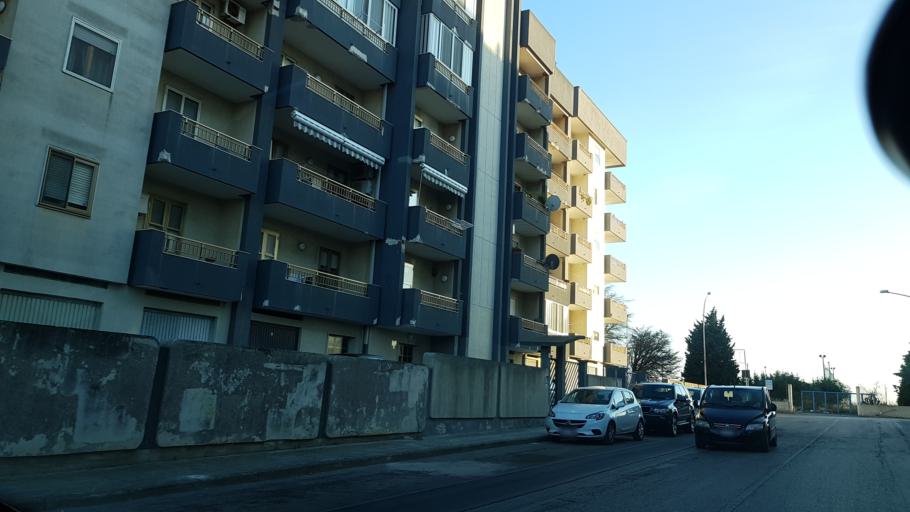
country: IT
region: Apulia
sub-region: Provincia di Brindisi
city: Brindisi
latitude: 40.6178
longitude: 17.9330
